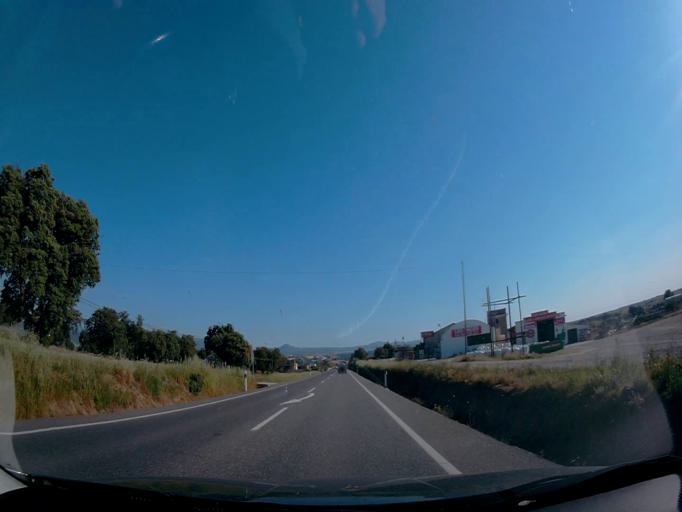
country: ES
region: Castille-La Mancha
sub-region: Province of Toledo
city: Escalona
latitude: 40.1372
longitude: -4.4041
